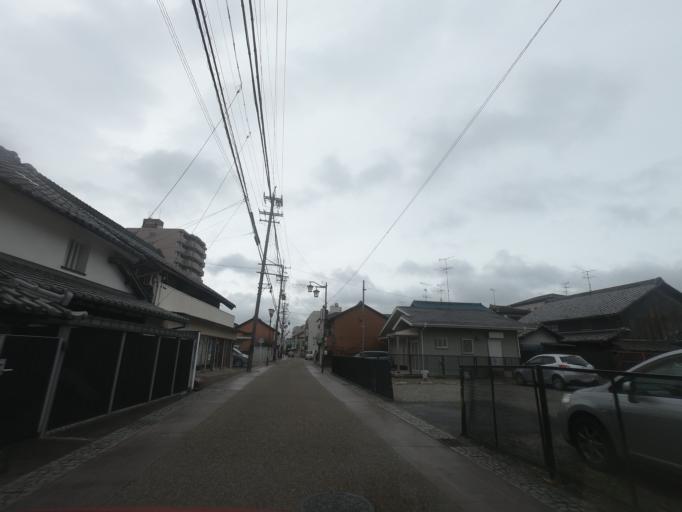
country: JP
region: Aichi
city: Kasugai
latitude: 35.2467
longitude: 136.9771
